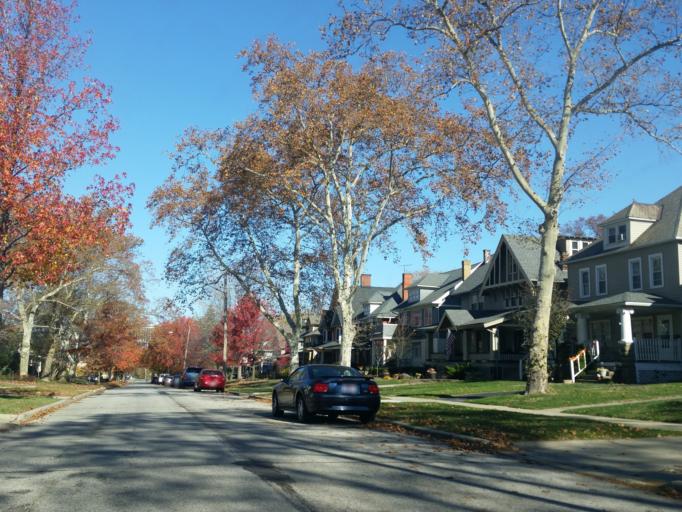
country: US
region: Ohio
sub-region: Cuyahoga County
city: Lakewood
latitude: 41.4813
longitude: -81.7791
